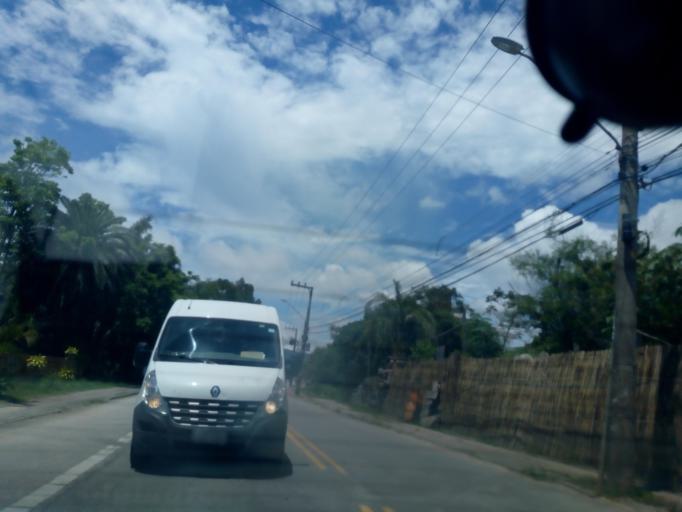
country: BR
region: Santa Catarina
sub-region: Florianopolis
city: Itacorubi
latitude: -27.4087
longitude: -48.4242
